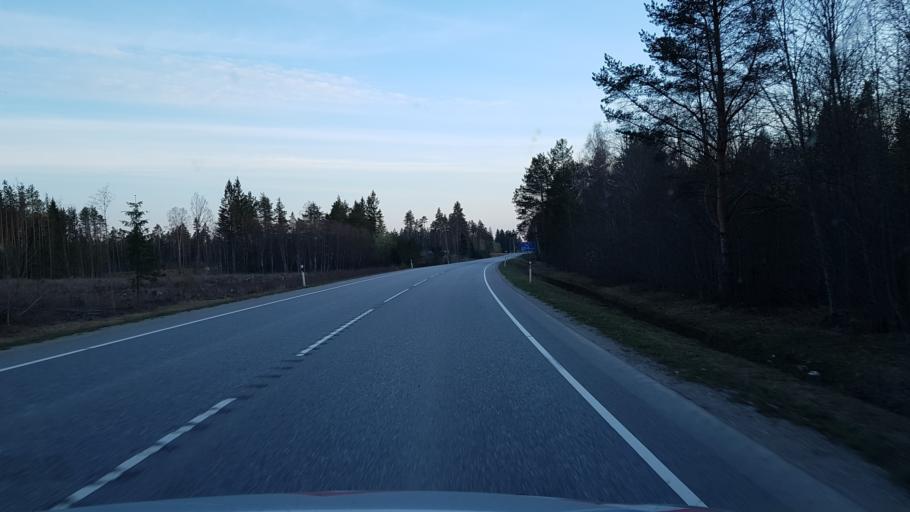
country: EE
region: Laeaene-Virumaa
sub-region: Someru vald
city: Someru
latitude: 59.3369
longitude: 26.4102
